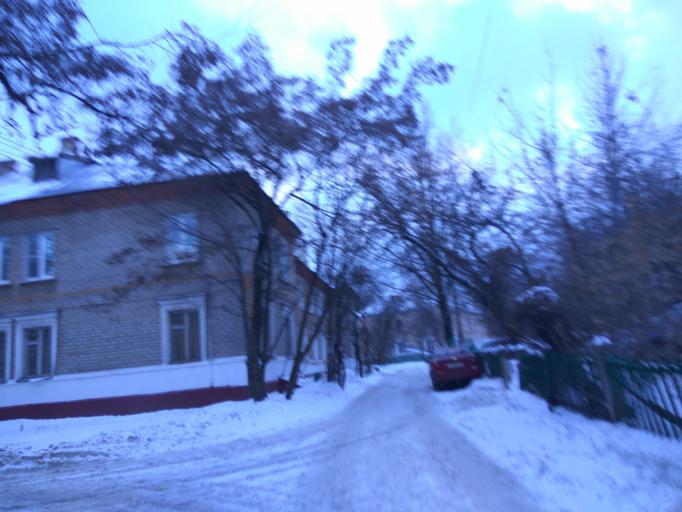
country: RU
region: Moskovskaya
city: Kur'yanovo
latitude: 55.6568
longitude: 37.7072
